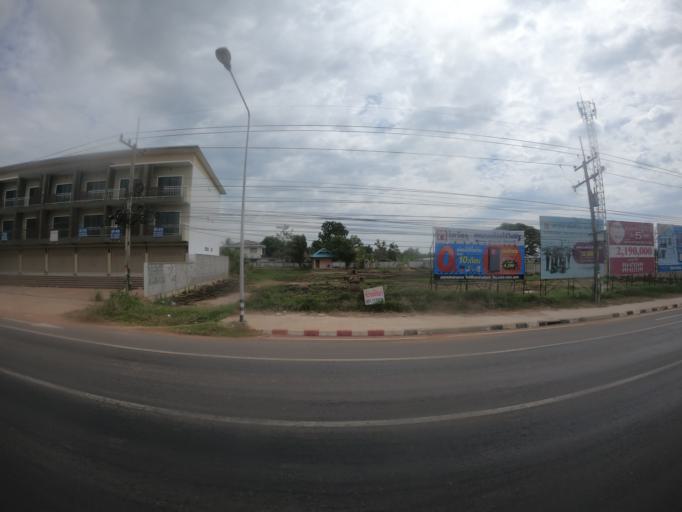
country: TH
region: Maha Sarakham
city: Maha Sarakham
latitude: 16.2478
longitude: 103.2739
